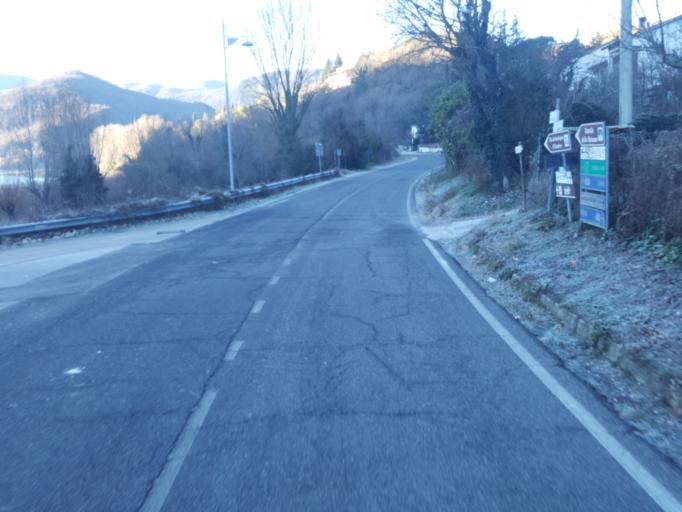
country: IT
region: Umbria
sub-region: Provincia di Terni
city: Arrone
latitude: 42.5424
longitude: 12.7557
